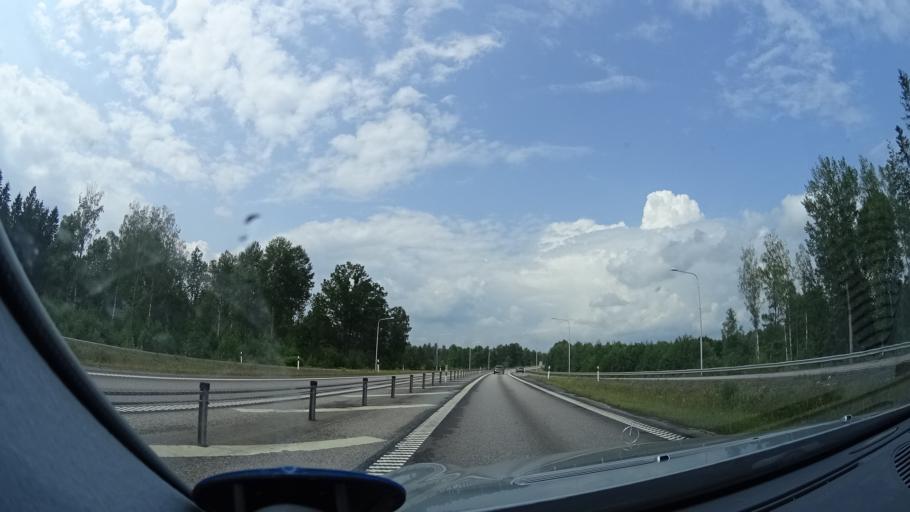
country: SE
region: Kalmar
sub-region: Nybro Kommun
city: Nybro
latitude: 56.7288
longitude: 15.8838
